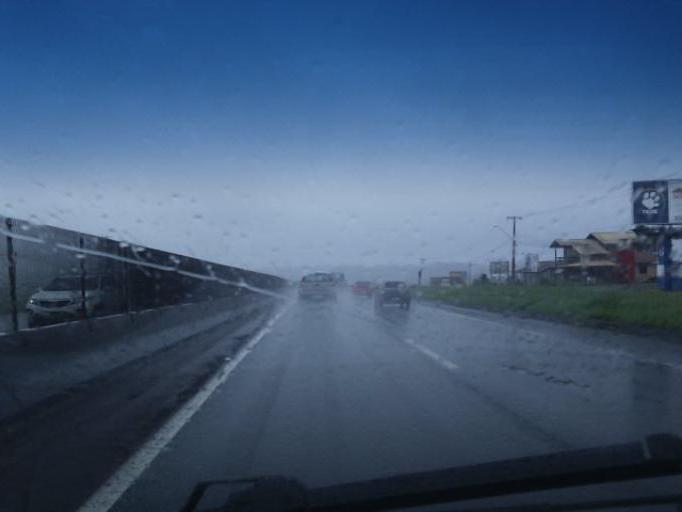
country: BR
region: Parana
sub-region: Sao Jose Dos Pinhais
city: Sao Jose dos Pinhais
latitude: -25.6103
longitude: -49.1718
